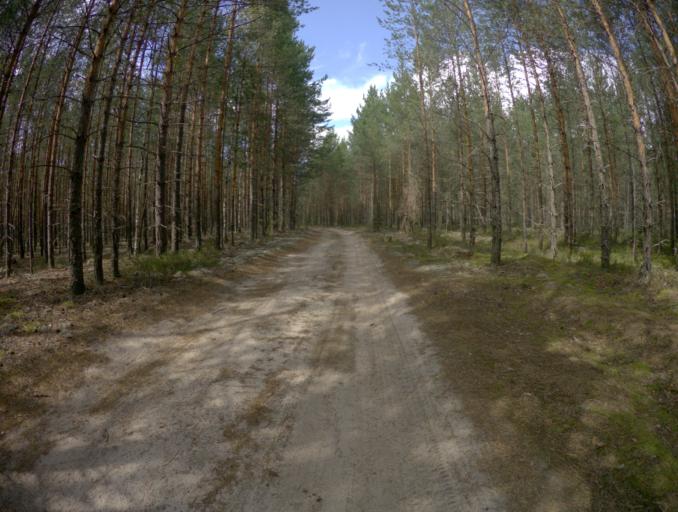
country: RU
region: Vladimir
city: Raduzhnyy
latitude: 55.9595
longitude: 40.2014
